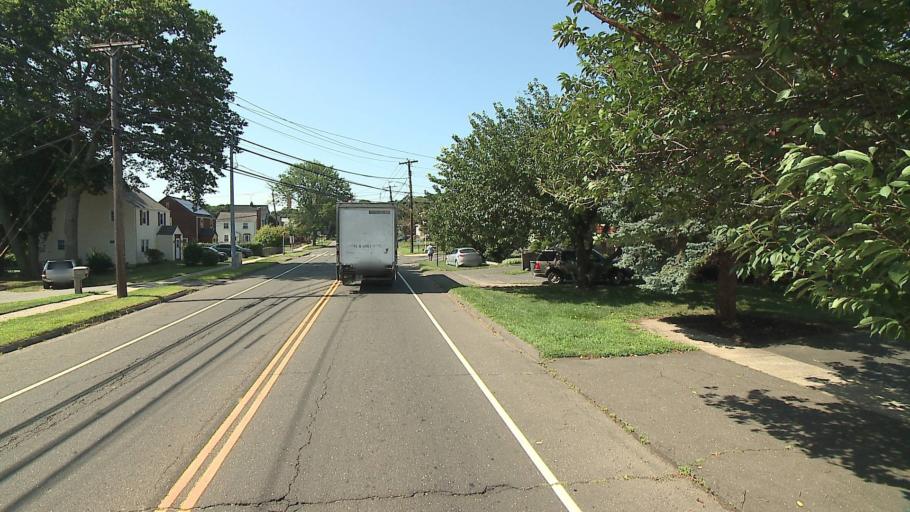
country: US
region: Connecticut
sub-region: Fairfield County
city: Stratford
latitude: 41.2162
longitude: -73.1252
